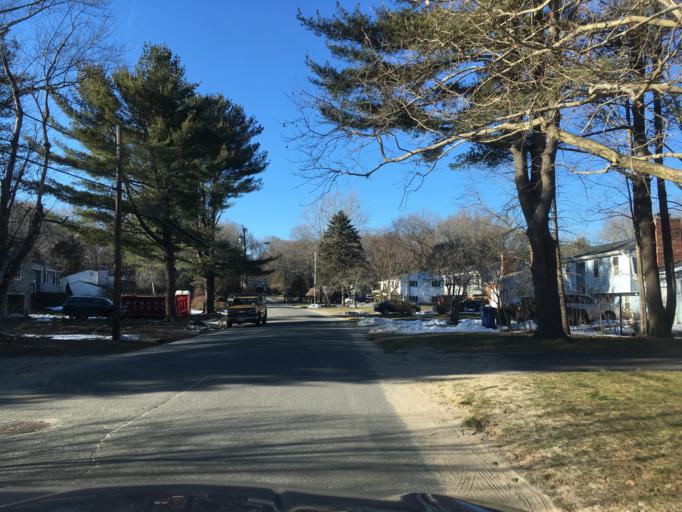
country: US
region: Rhode Island
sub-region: Kent County
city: East Greenwich
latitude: 41.6457
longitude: -71.4751
